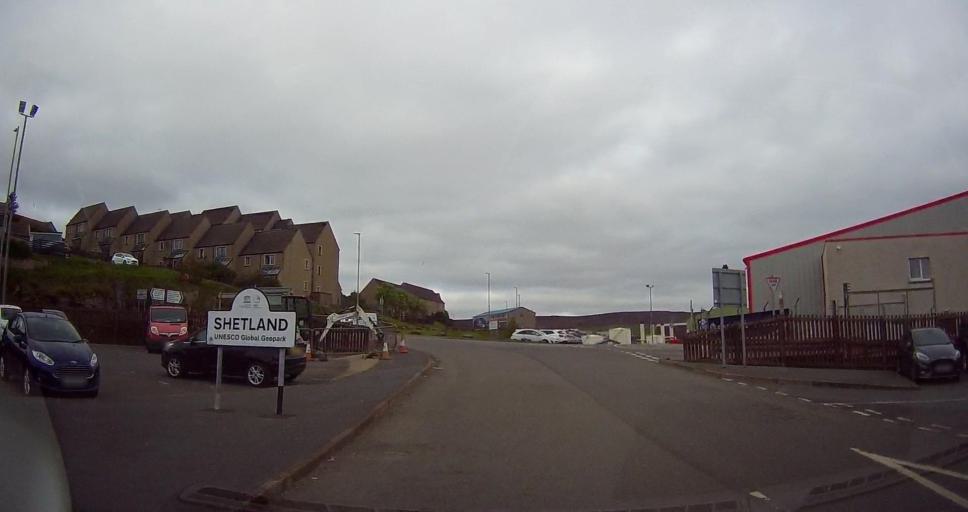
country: GB
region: Scotland
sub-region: Shetland Islands
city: Lerwick
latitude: 60.1633
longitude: -1.1592
